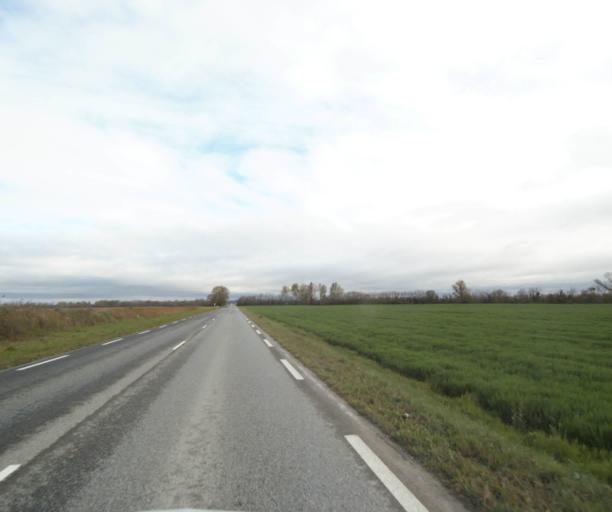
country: FR
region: Midi-Pyrenees
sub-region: Departement de l'Ariege
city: Saverdun
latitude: 43.2140
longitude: 1.6078
